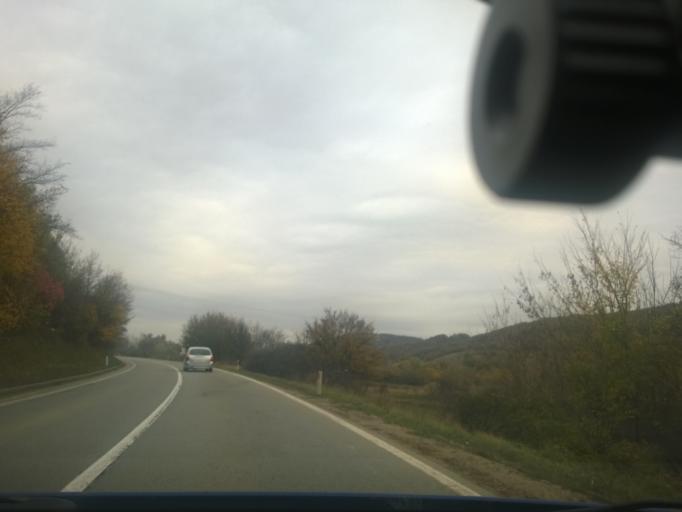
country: RS
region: Central Serbia
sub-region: Pirotski Okrug
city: Dimitrovgrad
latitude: 43.0328
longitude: 22.7192
